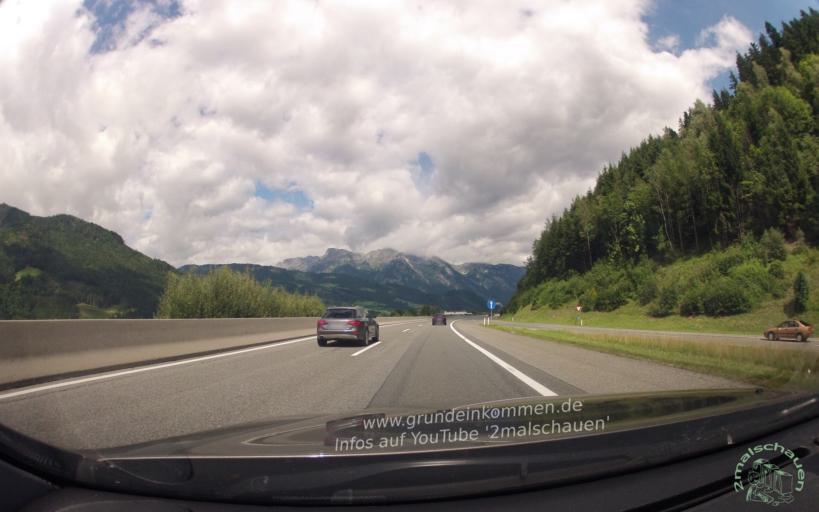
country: AT
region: Salzburg
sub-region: Politischer Bezirk Sankt Johann im Pongau
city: Pfarrwerfen
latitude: 47.4414
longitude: 13.2212
